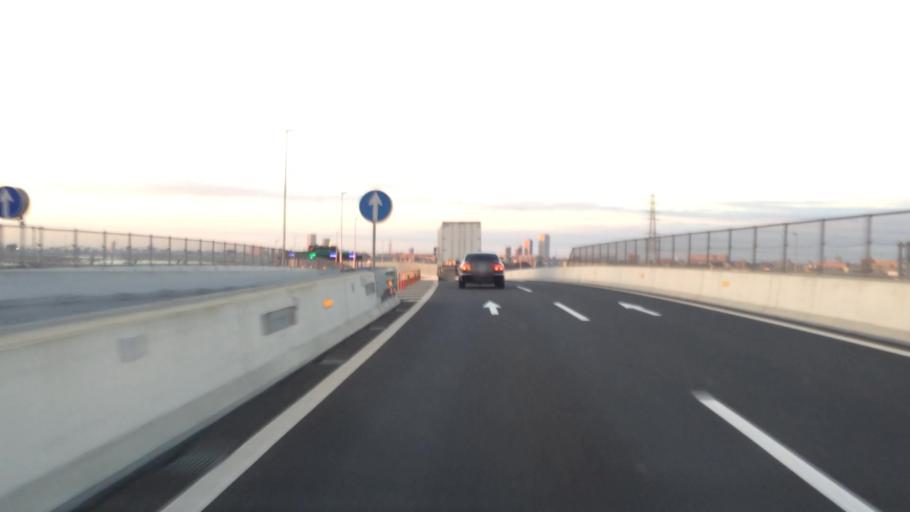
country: JP
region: Chiba
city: Funabashi
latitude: 35.6887
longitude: 139.9450
